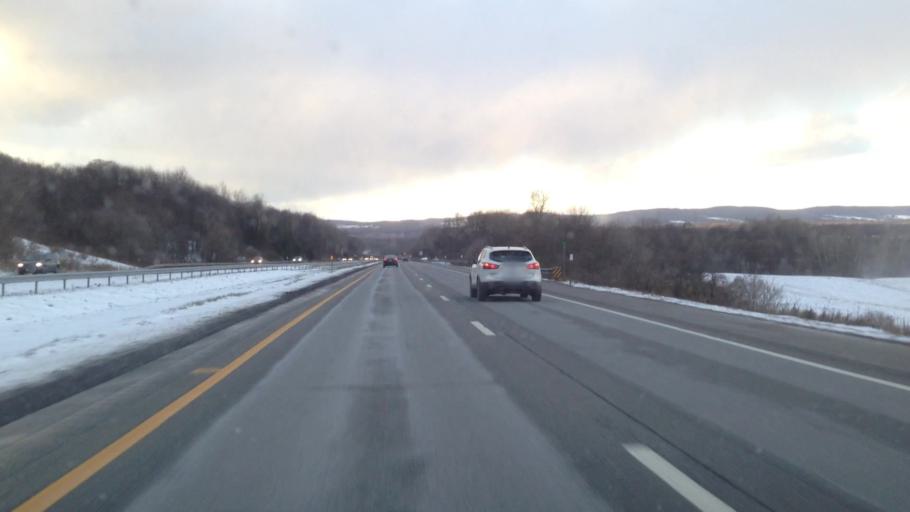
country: US
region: New York
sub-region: Herkimer County
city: Little Falls
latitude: 43.0083
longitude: -74.9064
